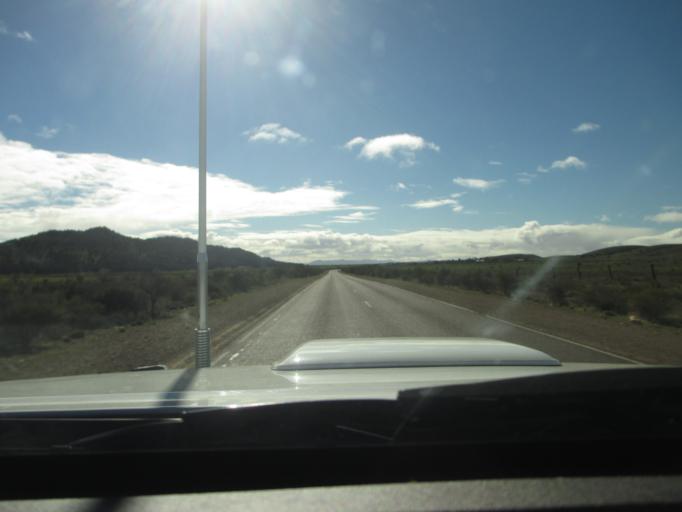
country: AU
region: South Australia
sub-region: Flinders Ranges
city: Quorn
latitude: -31.9433
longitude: 138.4021
